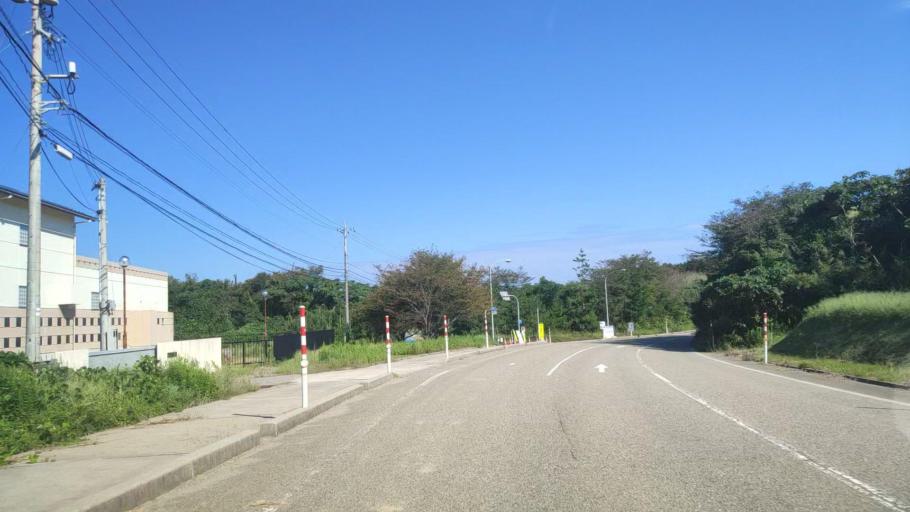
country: JP
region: Ishikawa
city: Hakui
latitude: 37.0729
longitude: 136.7216
